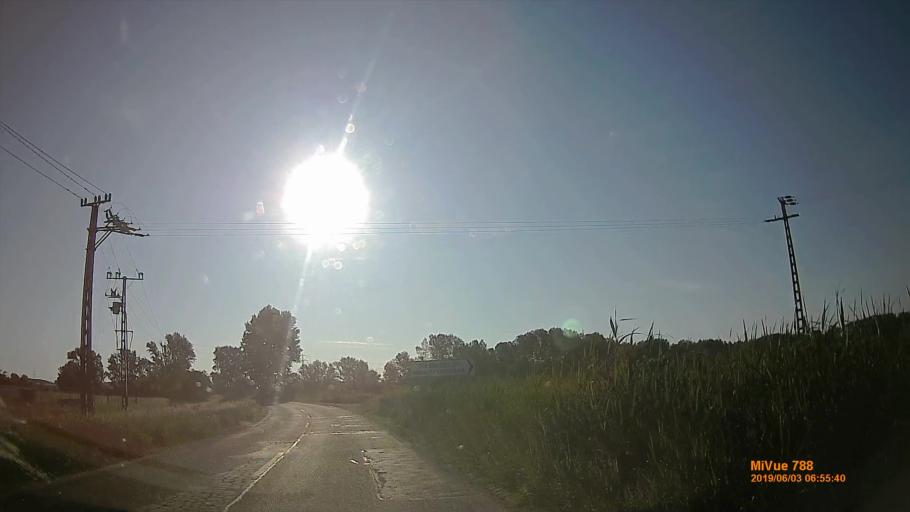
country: HU
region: Pest
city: Dabas
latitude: 47.2169
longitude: 19.2478
